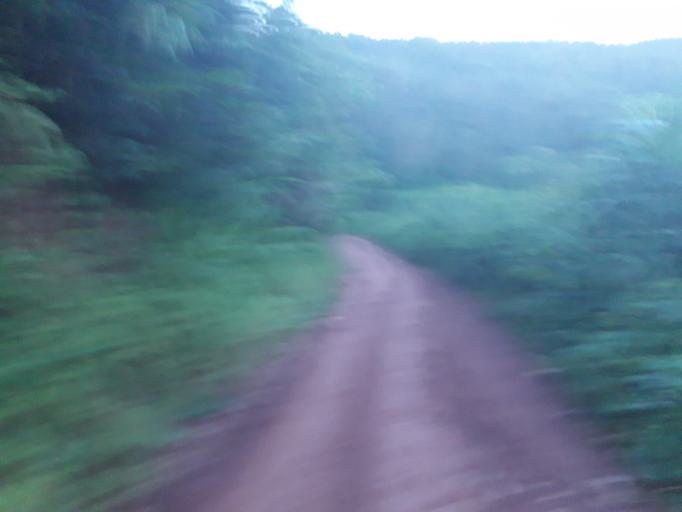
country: CN
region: Yunnan
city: Menglie
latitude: 22.1212
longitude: 101.7739
